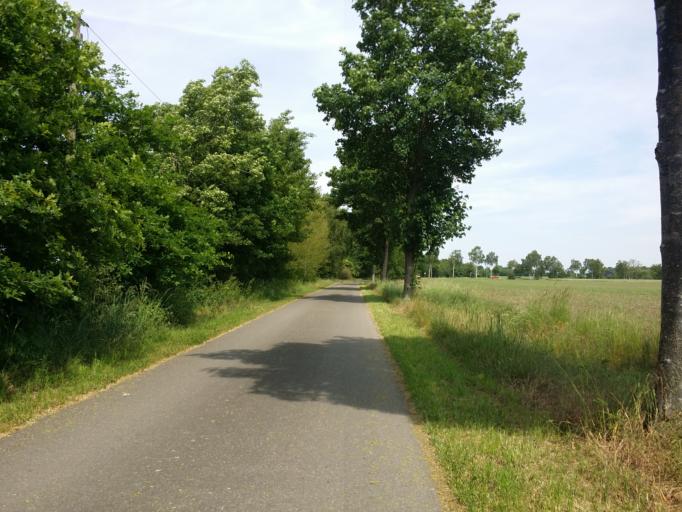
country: DE
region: Lower Saxony
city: Syke
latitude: 52.9675
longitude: 8.8656
